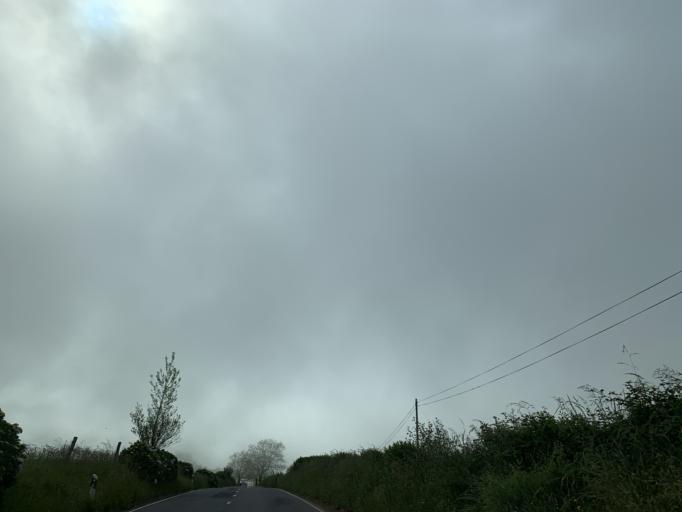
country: PT
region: Azores
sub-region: Ponta Delgada
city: Arrifes
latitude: 37.7748
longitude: -25.7468
